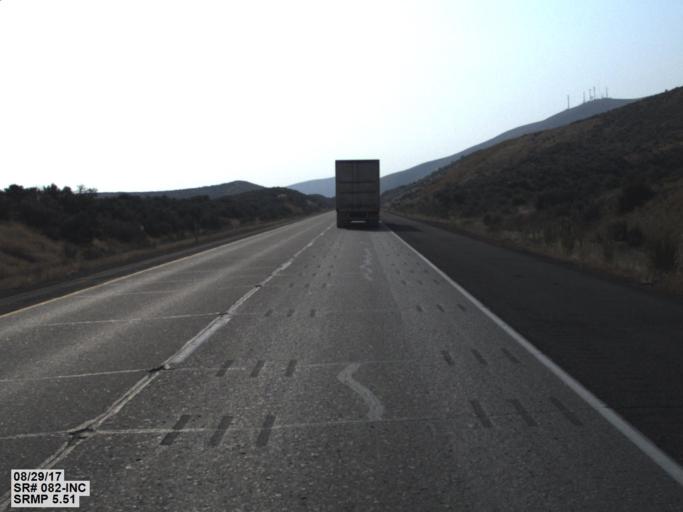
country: US
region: Washington
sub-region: Kittitas County
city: Kittitas
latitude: 46.9062
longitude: -120.4617
